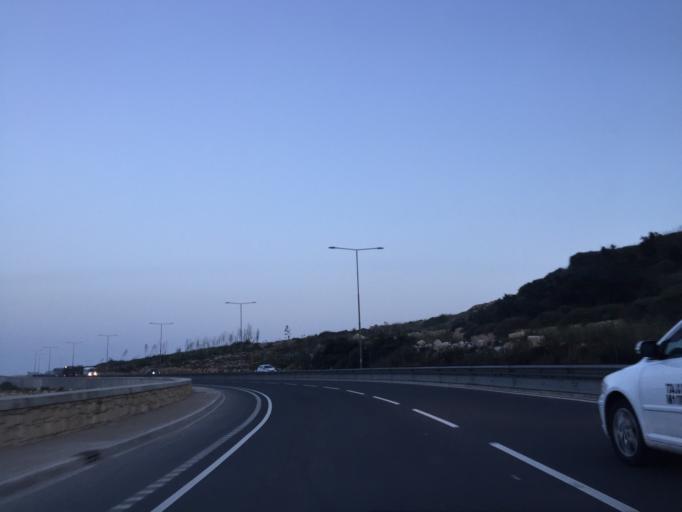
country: MT
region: Hal Gharghur
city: Hal Gharghur
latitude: 35.9480
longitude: 14.4455
